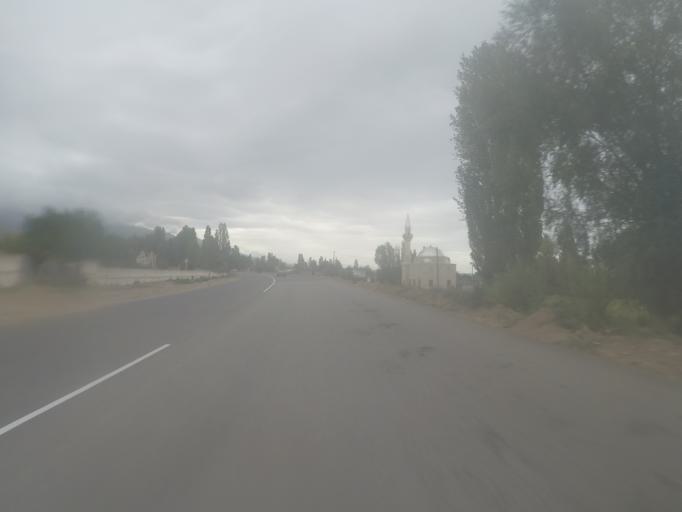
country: KG
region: Ysyk-Koel
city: Cholpon-Ata
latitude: 42.6695
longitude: 77.2900
